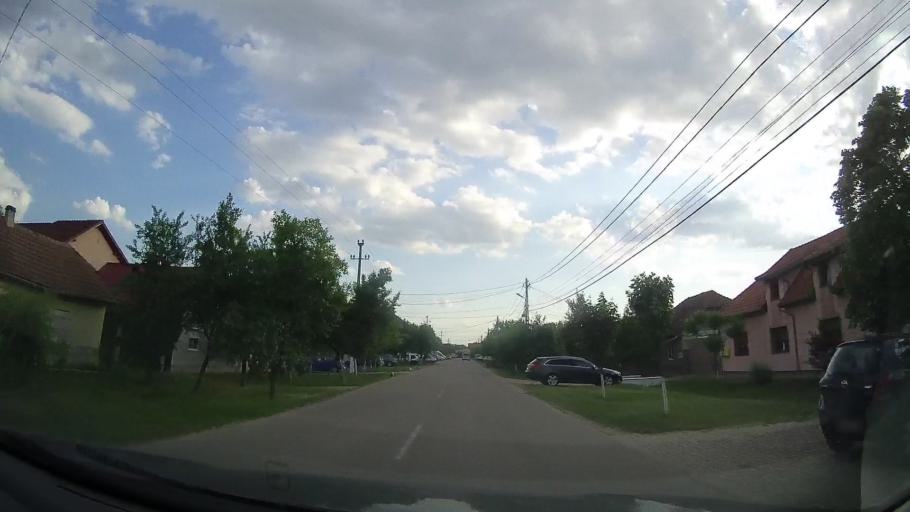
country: RO
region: Timis
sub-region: Comuna Dumbravita
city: Dumbravita
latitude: 45.7977
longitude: 21.2467
